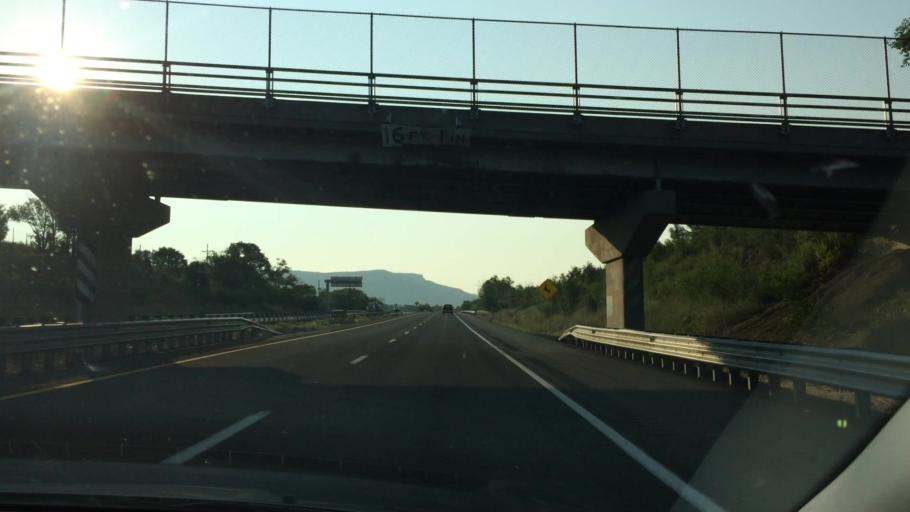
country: US
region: New Mexico
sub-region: Colfax County
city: Raton
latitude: 36.9135
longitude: -104.4350
